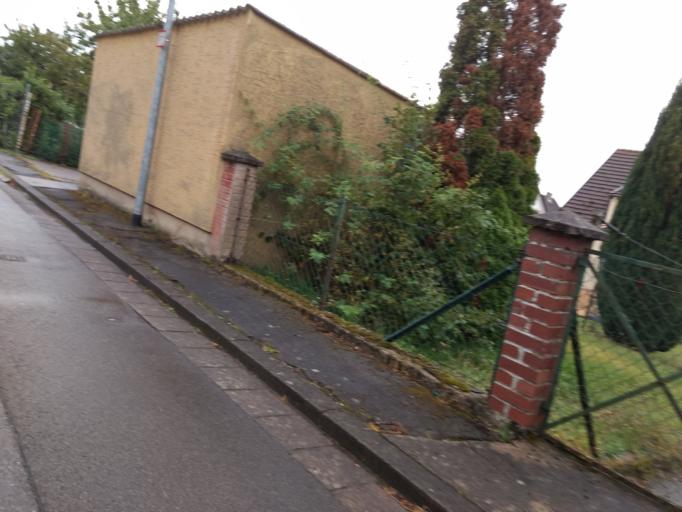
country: DE
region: Saarland
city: Dillingen
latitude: 49.3622
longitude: 6.7349
